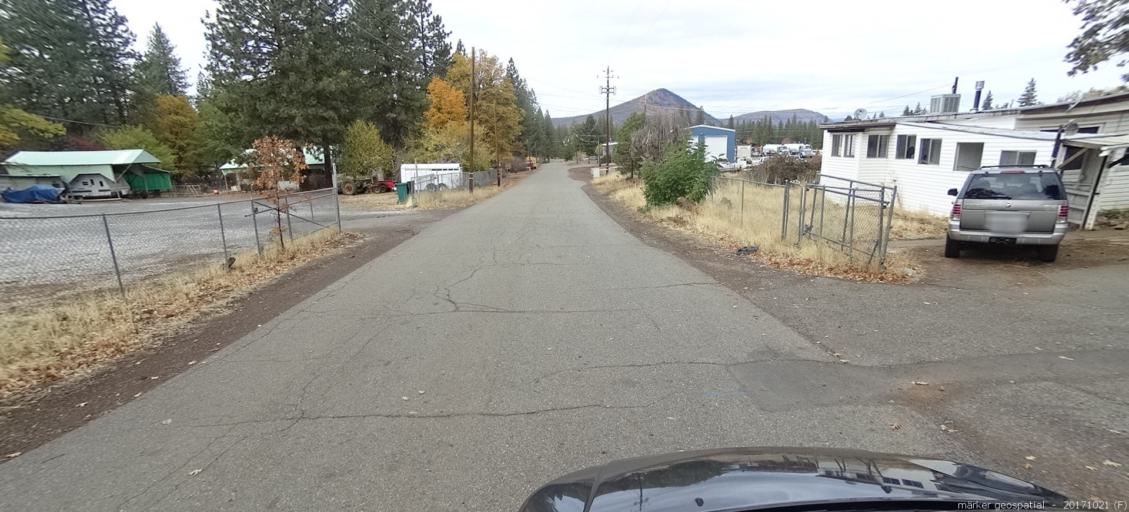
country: US
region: California
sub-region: Shasta County
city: Burney
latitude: 40.9188
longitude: -121.6264
